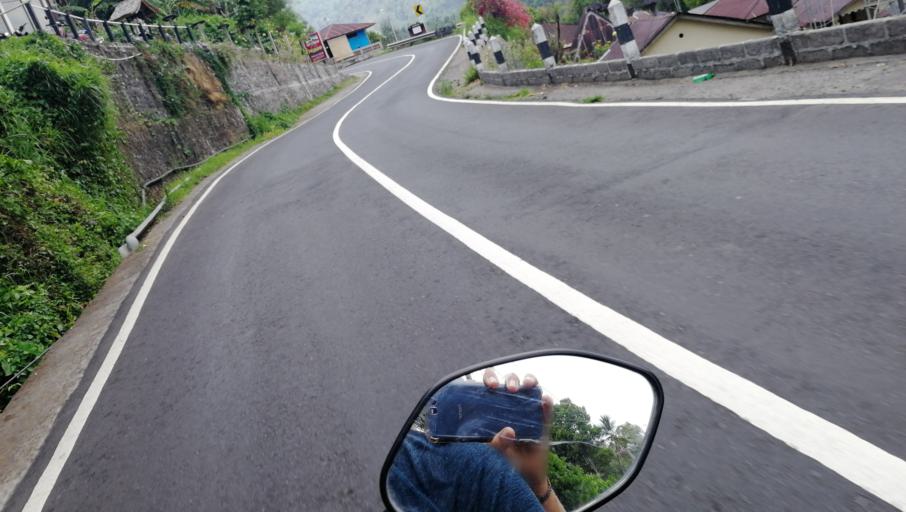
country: ID
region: Bali
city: Munduk
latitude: -8.2647
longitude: 115.0597
